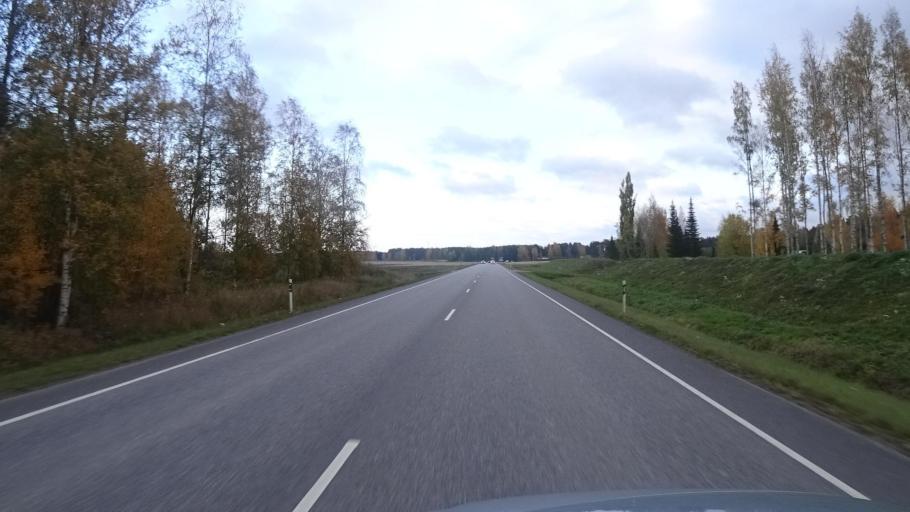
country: FI
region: Satakunta
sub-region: Rauma
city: Saekylae
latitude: 61.0422
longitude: 22.3747
